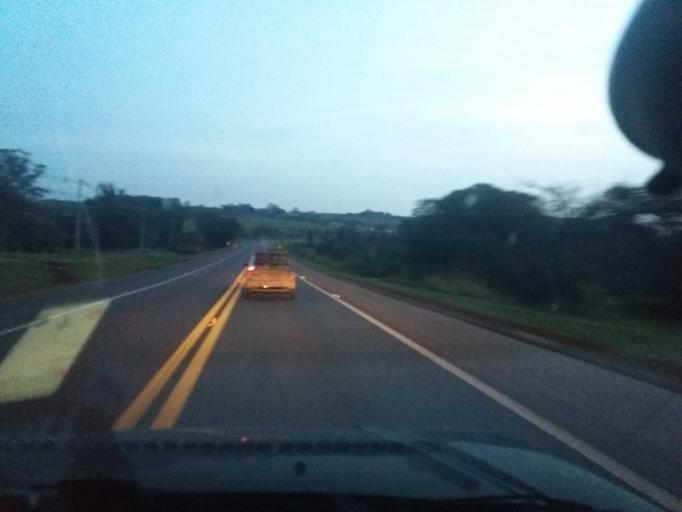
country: BR
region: Sao Paulo
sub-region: Itapeva
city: Itapeva
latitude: -23.9765
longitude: -48.8442
